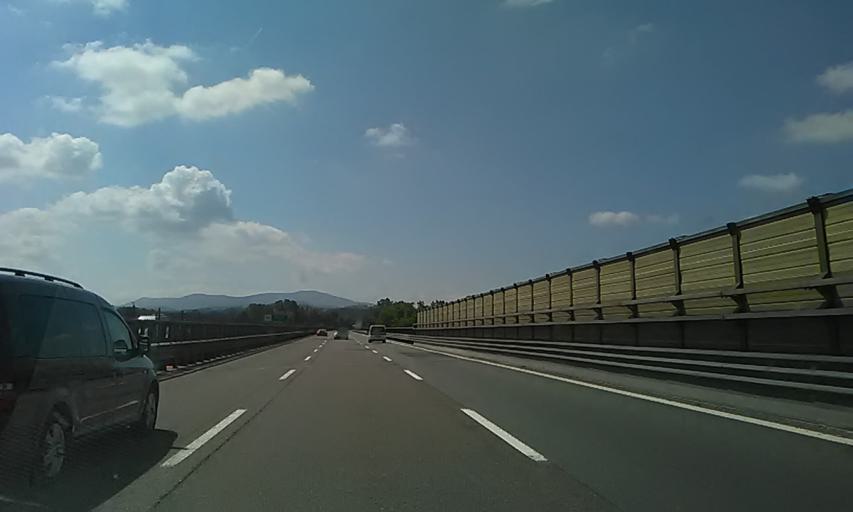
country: IT
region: Piedmont
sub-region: Provincia di Alessandria
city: Rocca Grimalda
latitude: 44.6742
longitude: 8.6584
